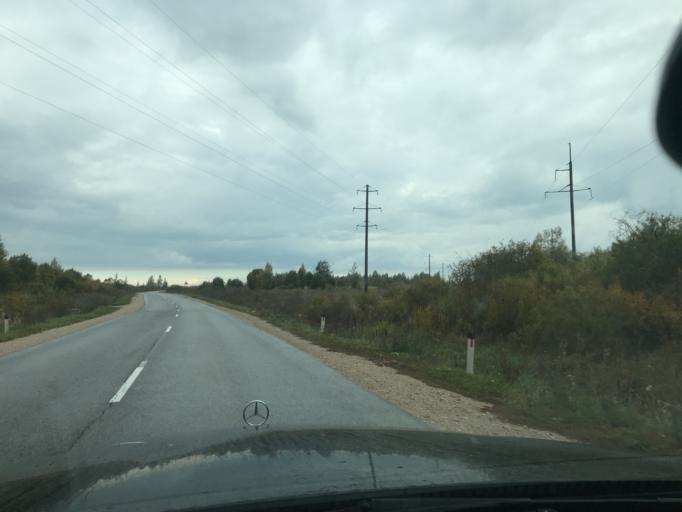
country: RU
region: Pskov
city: Izborsk
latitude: 57.6261
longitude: 27.9152
